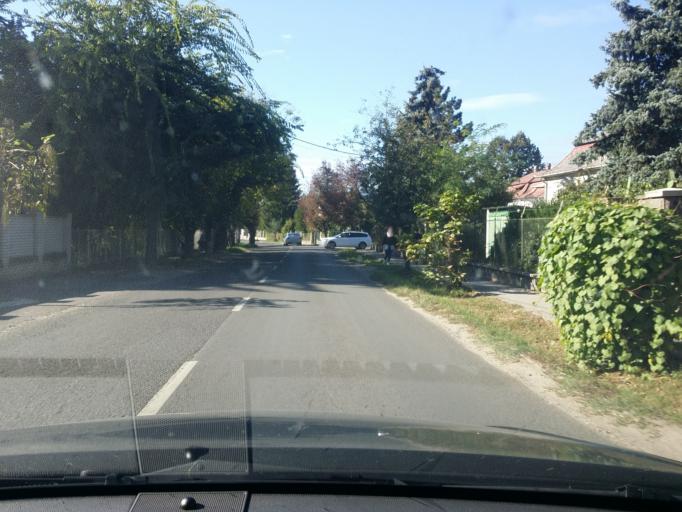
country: HU
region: Pest
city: God
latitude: 47.7061
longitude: 19.1413
